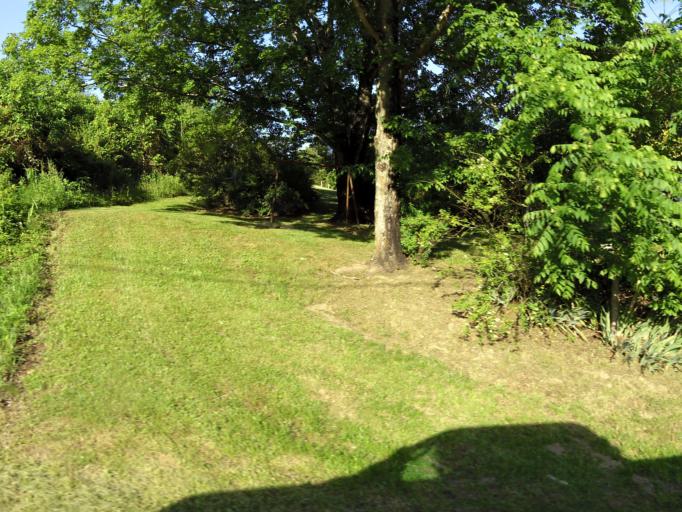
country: US
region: Tennessee
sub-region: Sevier County
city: Sevierville
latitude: 35.8406
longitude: -83.6220
